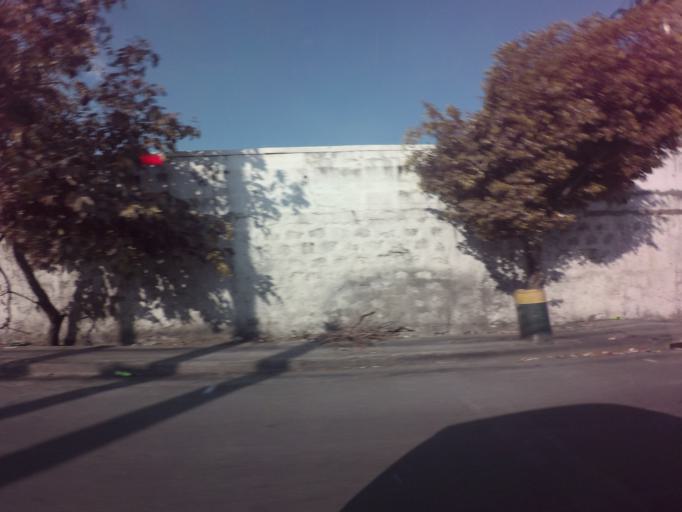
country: PH
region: Calabarzon
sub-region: Province of Rizal
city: Taguig
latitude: 14.4804
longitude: 121.0502
